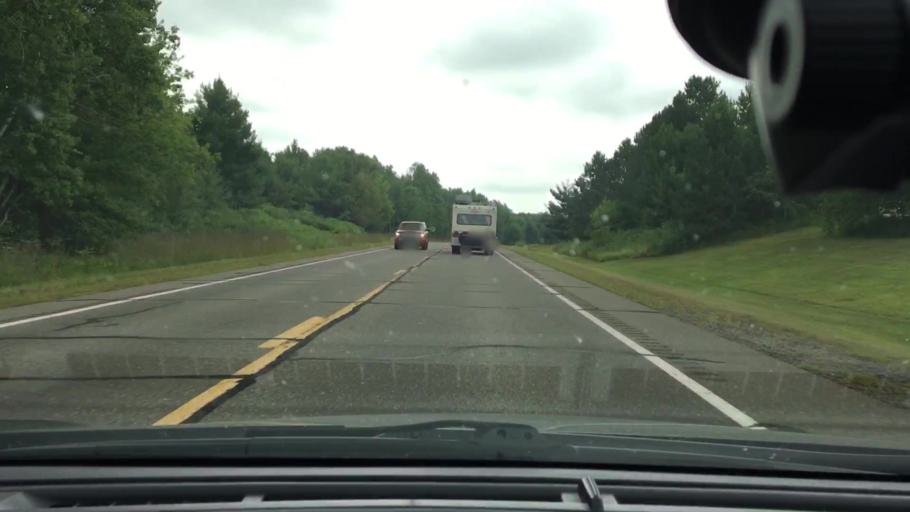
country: US
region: Minnesota
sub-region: Crow Wing County
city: Crosby
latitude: 46.4373
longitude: -93.8748
